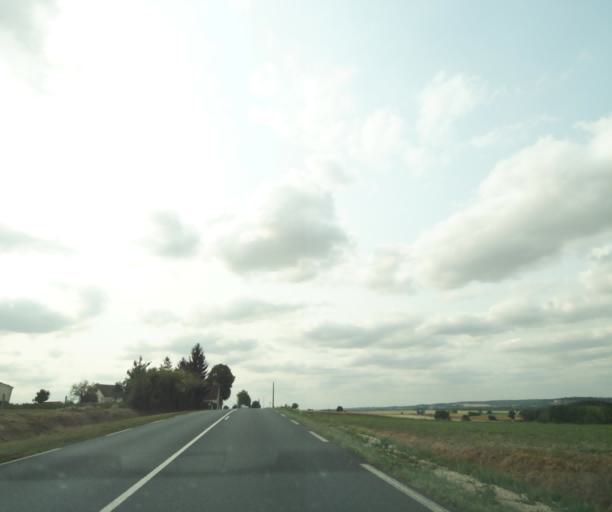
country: FR
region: Centre
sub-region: Departement de l'Indre
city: Buzancais
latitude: 46.9109
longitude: 1.3351
